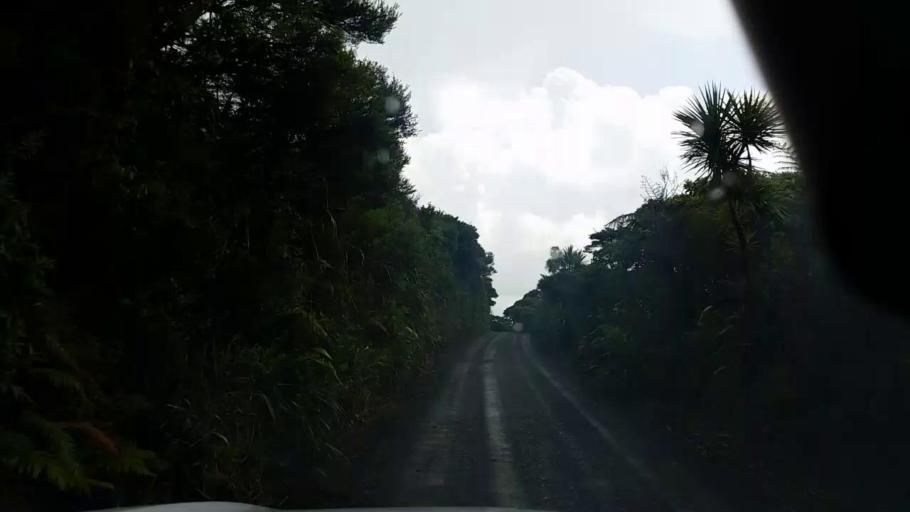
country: NZ
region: Auckland
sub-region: Auckland
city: Muriwai Beach
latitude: -36.9274
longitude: 174.4785
